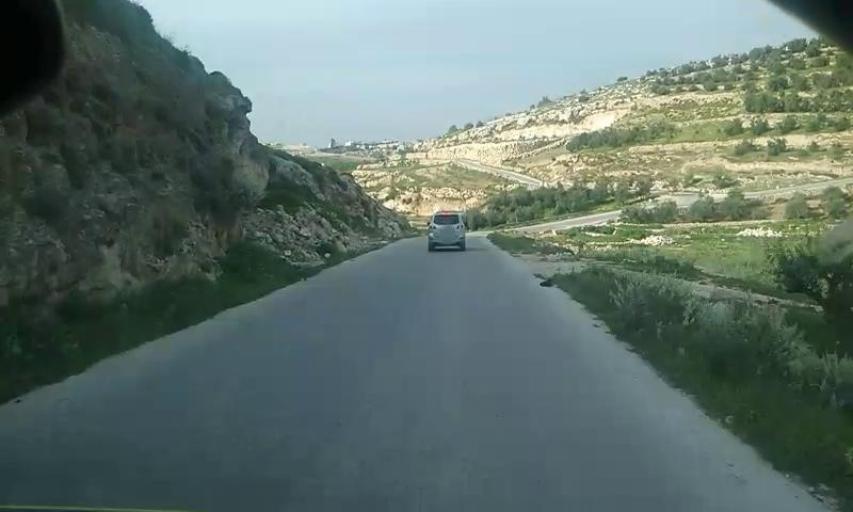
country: PS
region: West Bank
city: Nuba
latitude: 31.6135
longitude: 35.0189
